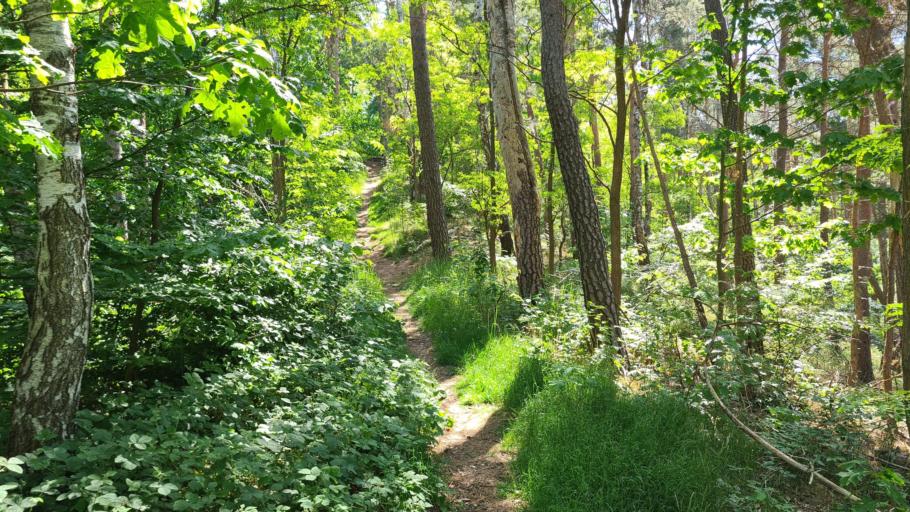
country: DE
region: Brandenburg
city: Grosskmehlen
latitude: 51.3652
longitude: 13.7256
